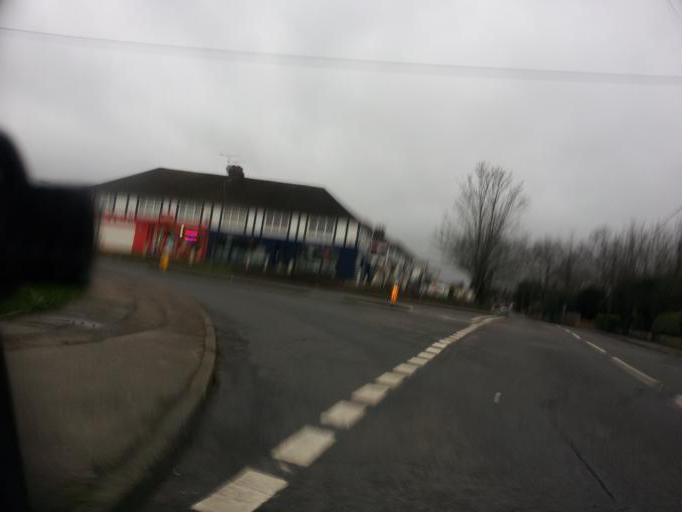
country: GB
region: England
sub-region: Kent
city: Longfield
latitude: 51.3888
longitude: 0.3045
